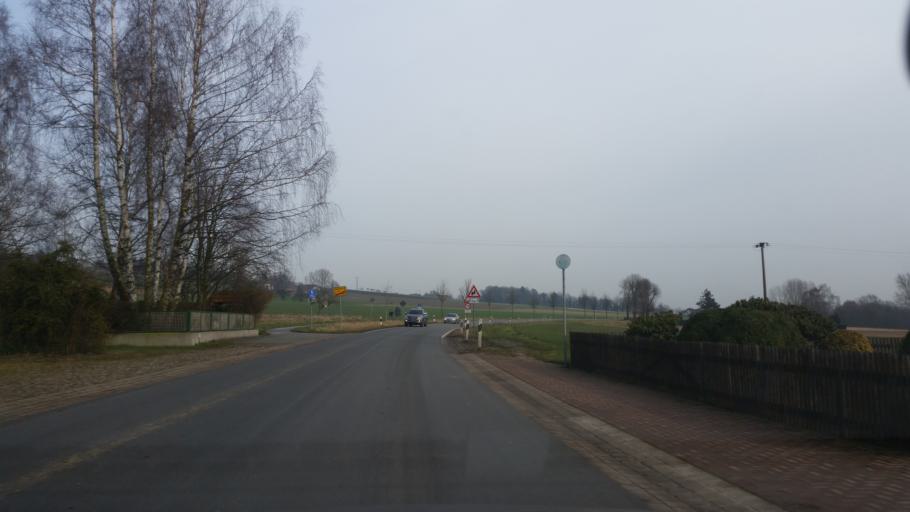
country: DE
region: Lower Saxony
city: Aerzen
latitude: 52.0742
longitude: 9.2303
